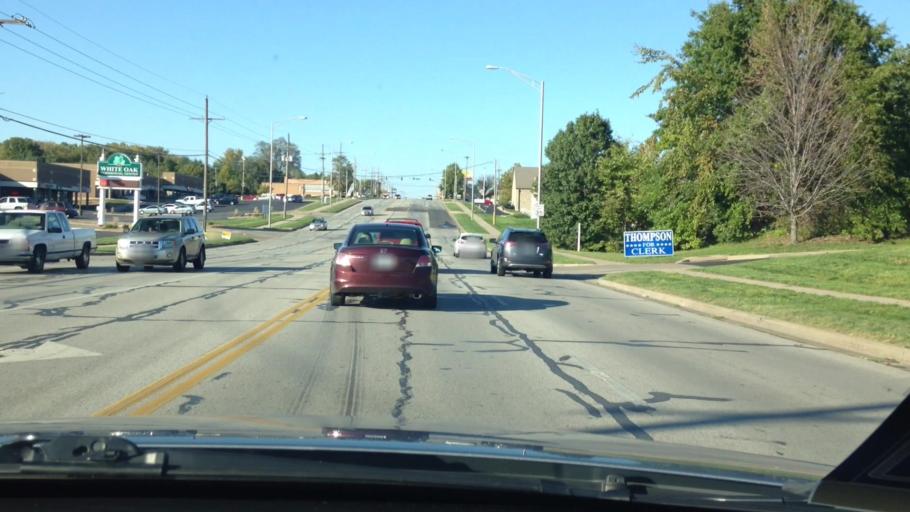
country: US
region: Missouri
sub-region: Clay County
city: Gladstone
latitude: 39.2383
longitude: -94.5760
